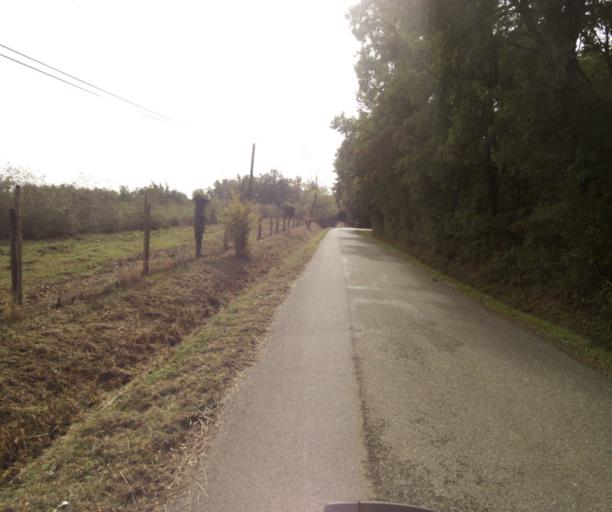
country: FR
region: Midi-Pyrenees
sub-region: Departement du Tarn-et-Garonne
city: Finhan
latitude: 43.9302
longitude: 1.2493
